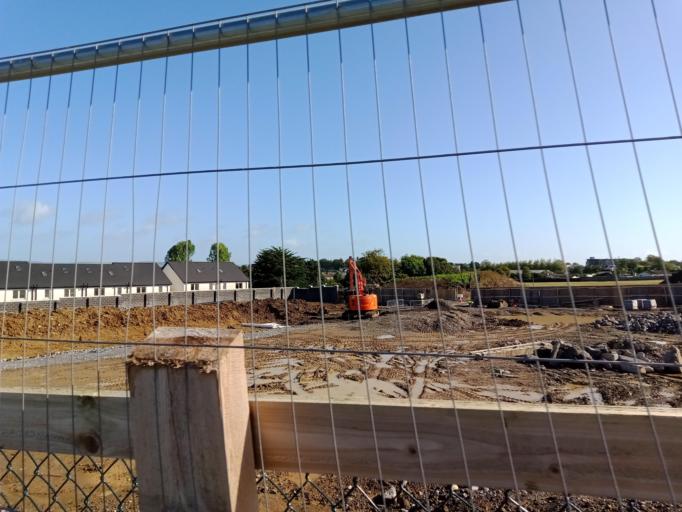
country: IE
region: Leinster
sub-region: Kilkenny
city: Kilkenny
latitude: 52.6446
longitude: -7.2688
